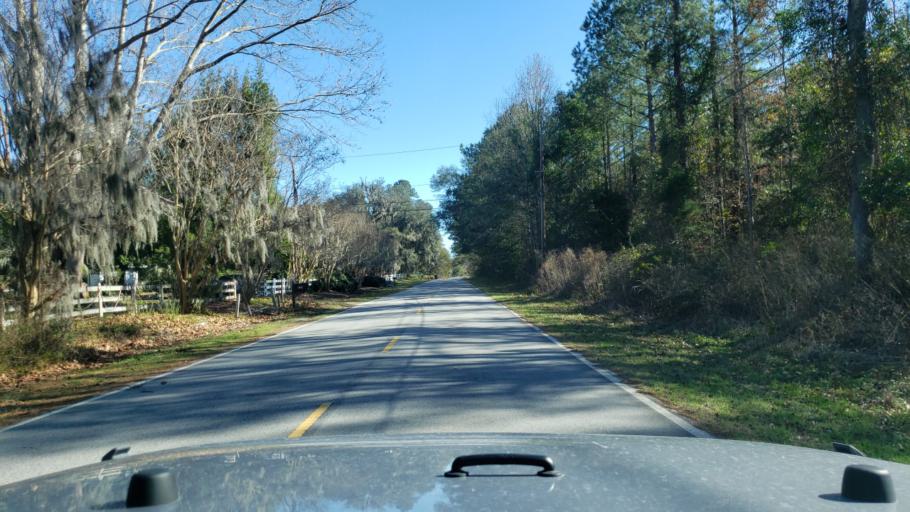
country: US
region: Georgia
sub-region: Chatham County
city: Georgetown
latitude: 32.0327
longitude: -81.1863
